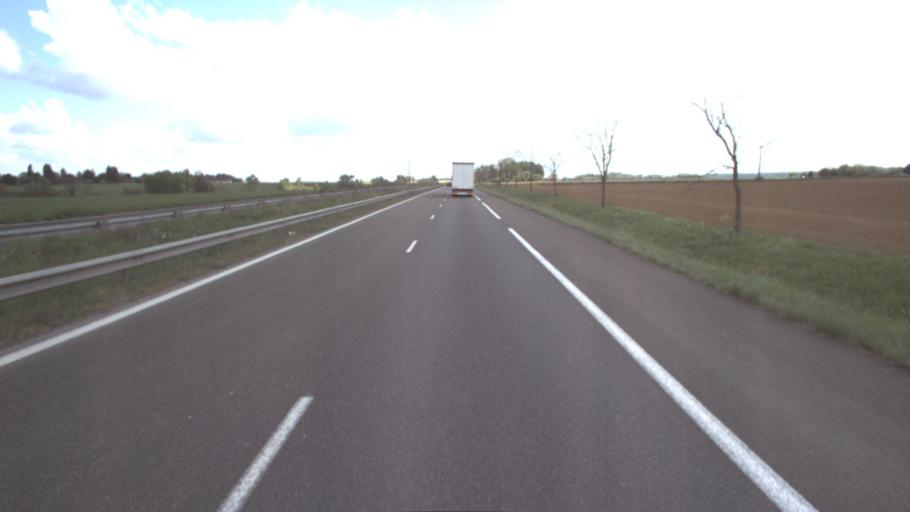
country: FR
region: Ile-de-France
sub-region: Departement de Seine-et-Marne
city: Rozay-en-Brie
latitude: 48.6861
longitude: 2.9941
